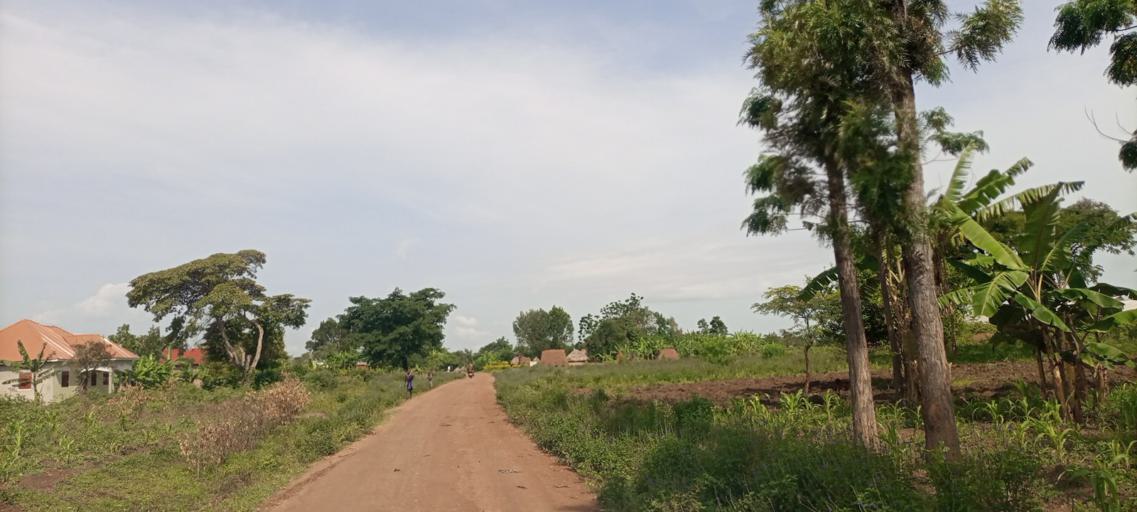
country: UG
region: Eastern Region
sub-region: Mbale District
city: Mbale
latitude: 1.1328
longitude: 34.0510
